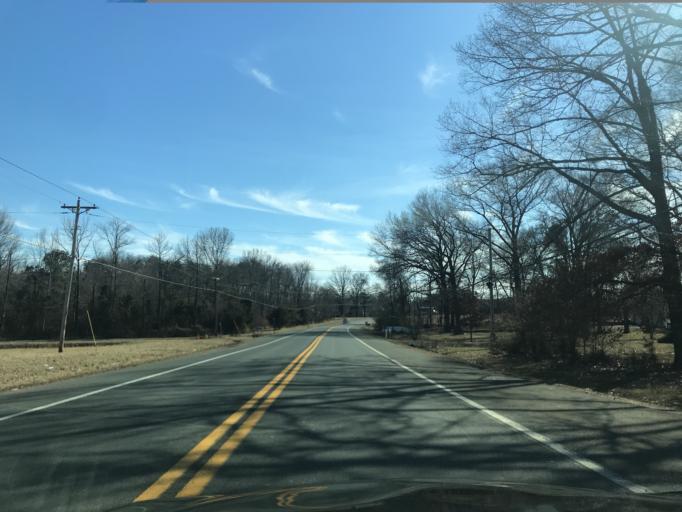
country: US
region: Maryland
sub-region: Charles County
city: Bryans Road
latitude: 38.6414
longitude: -77.0714
